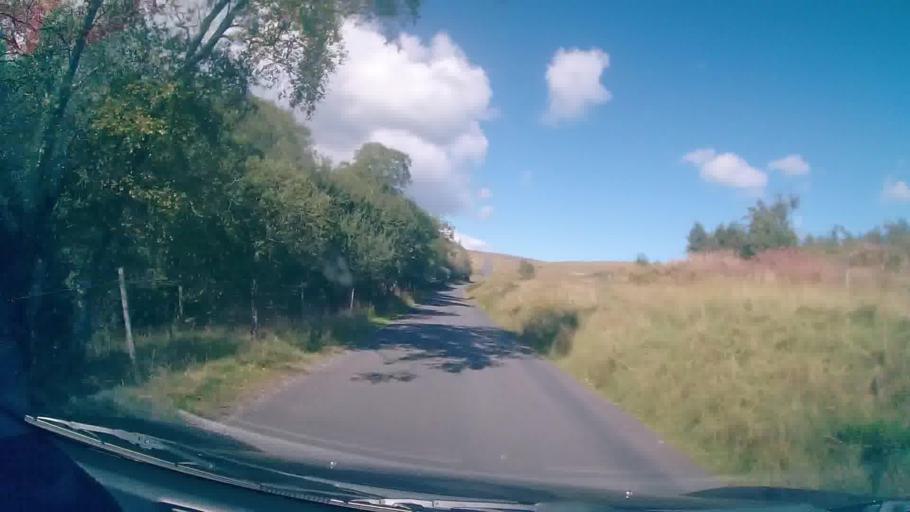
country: GB
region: Wales
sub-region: Merthyr Tydfil County Borough
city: Merthyr Tydfil
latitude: 51.8422
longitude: -3.3798
